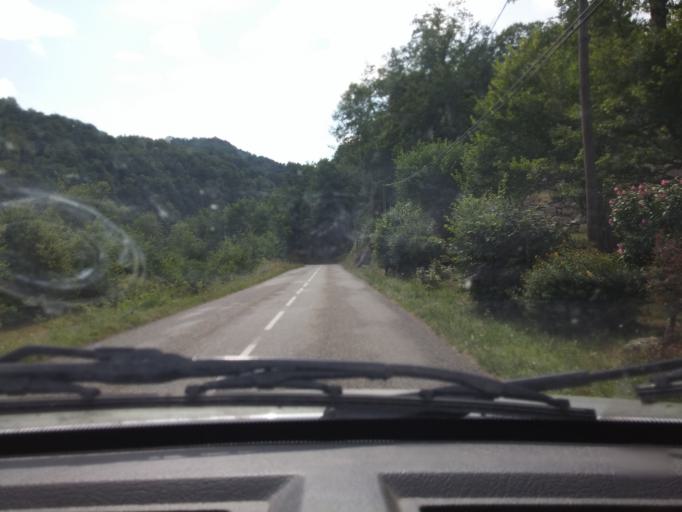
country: FR
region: Midi-Pyrenees
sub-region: Departement de l'Ariege
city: Saint-Girons
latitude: 42.8605
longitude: 1.2522
